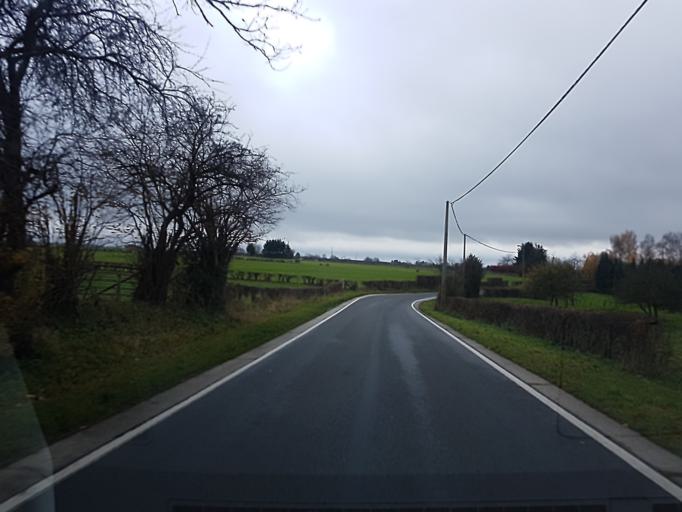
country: BE
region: Wallonia
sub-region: Province de Liege
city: Jalhay
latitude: 50.5688
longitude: 5.9684
